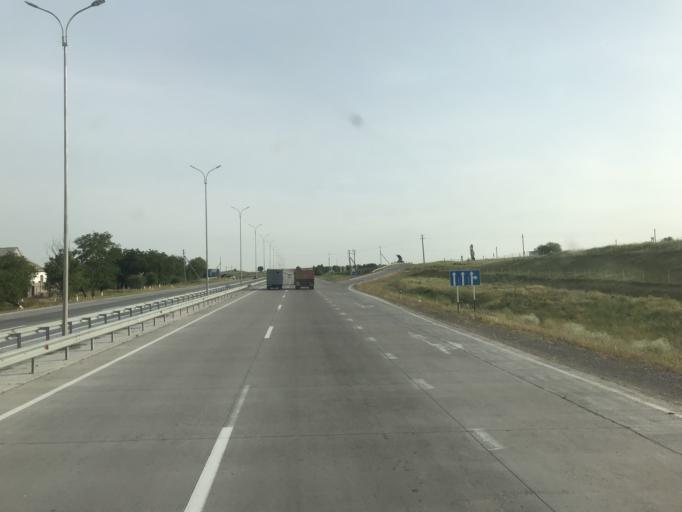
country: UZ
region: Toshkent
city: Qibray
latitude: 41.5642
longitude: 69.4084
